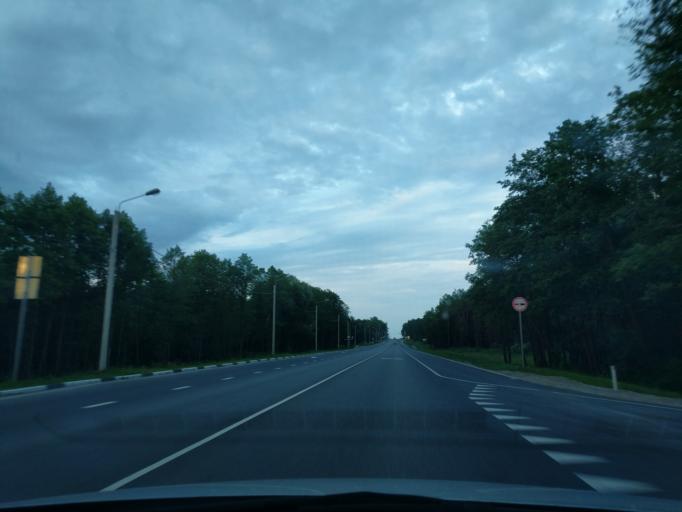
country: RU
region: Kaluga
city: Medyn'
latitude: 54.9712
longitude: 36.0466
